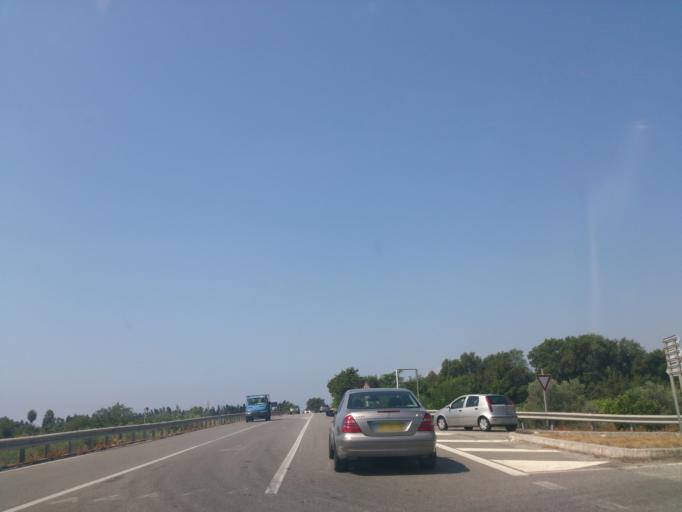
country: IT
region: Calabria
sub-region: Provincia di Reggio Calabria
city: Caulonia Marina
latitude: 38.3572
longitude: 16.4859
